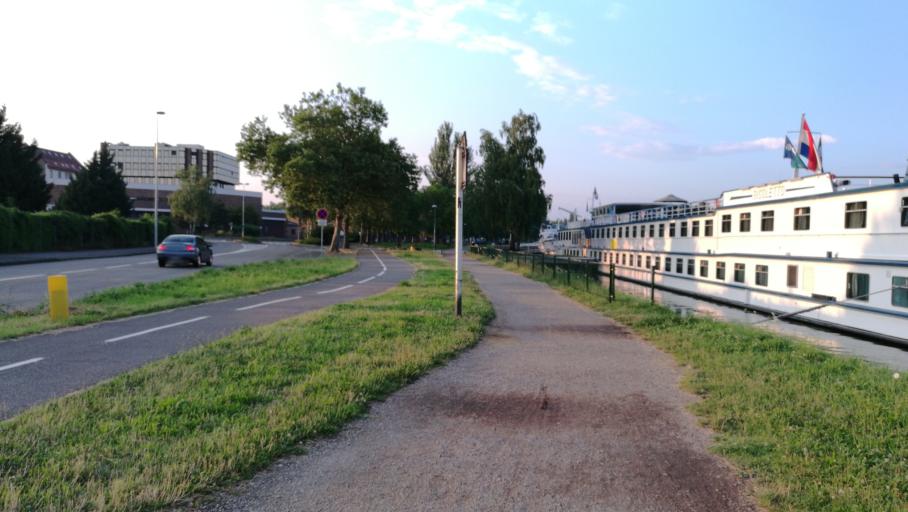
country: DE
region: Baden-Wuerttemberg
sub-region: Freiburg Region
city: Kehl
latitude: 48.5800
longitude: 7.7818
